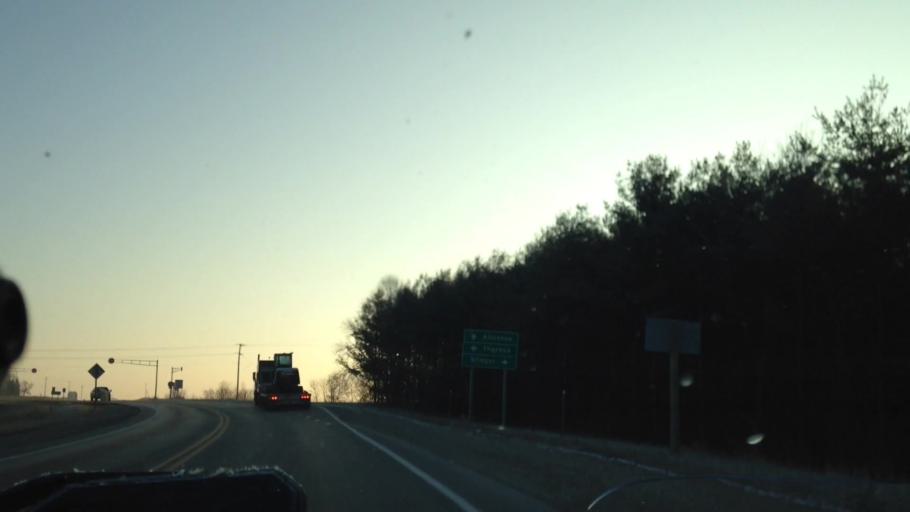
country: US
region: Wisconsin
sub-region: Washington County
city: Hartford
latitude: 43.4215
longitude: -88.3775
